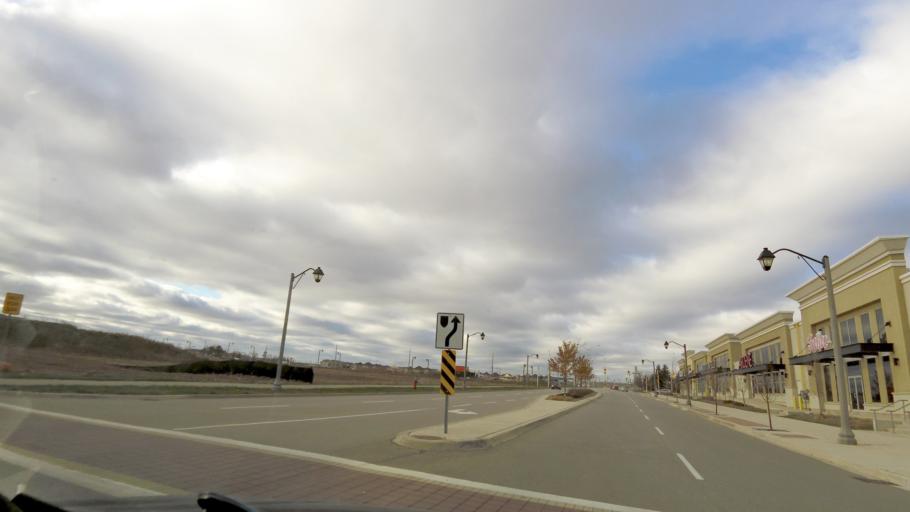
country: CA
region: Ontario
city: Oakville
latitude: 43.4820
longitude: -79.7210
